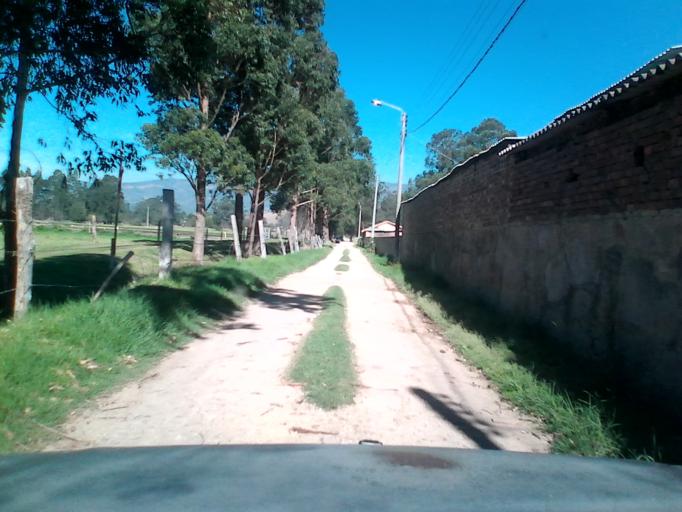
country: CO
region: Boyaca
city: Duitama
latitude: 5.7815
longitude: -73.0393
